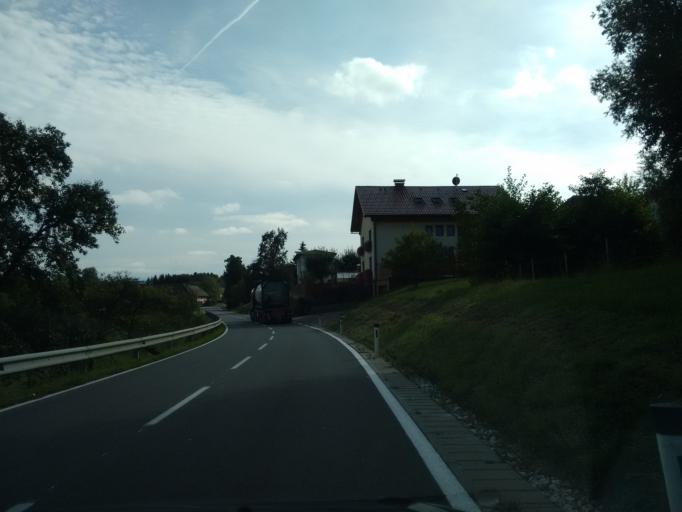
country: AT
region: Upper Austria
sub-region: Politischer Bezirk Steyr-Land
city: Bad Hall
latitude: 48.0912
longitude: 14.1924
